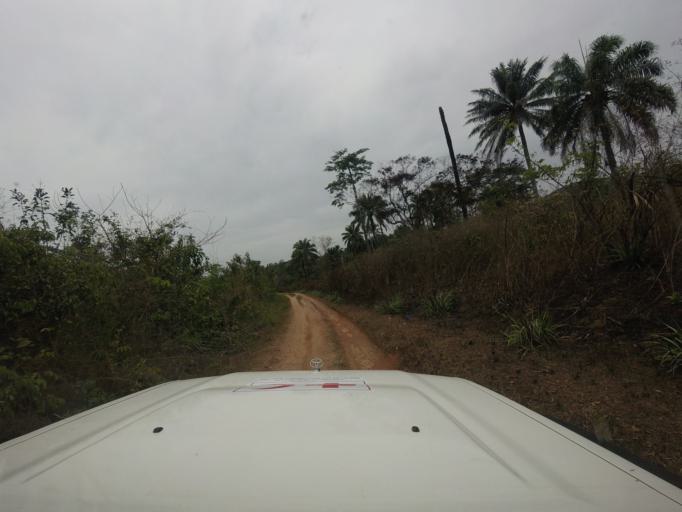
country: SL
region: Eastern Province
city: Buedu
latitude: 8.2714
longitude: -10.2862
